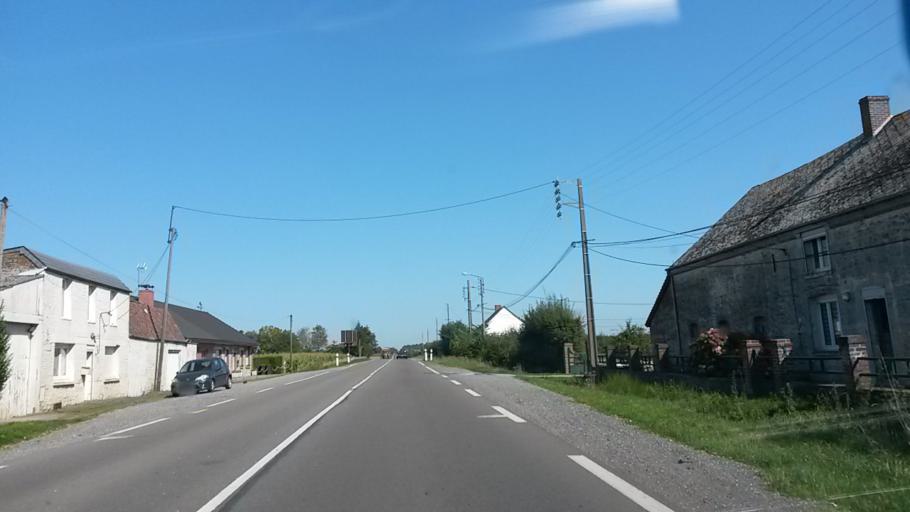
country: FR
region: Nord-Pas-de-Calais
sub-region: Departement du Nord
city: Avesnelles
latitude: 50.1783
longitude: 3.9526
